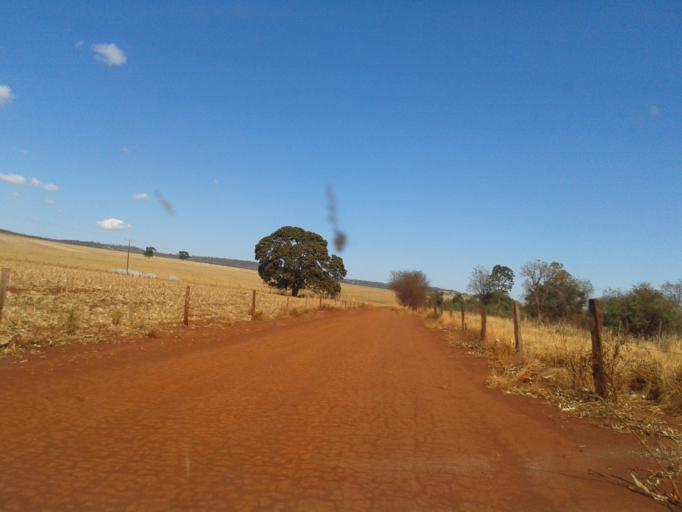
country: BR
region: Minas Gerais
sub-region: Centralina
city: Centralina
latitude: -18.5868
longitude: -49.1477
